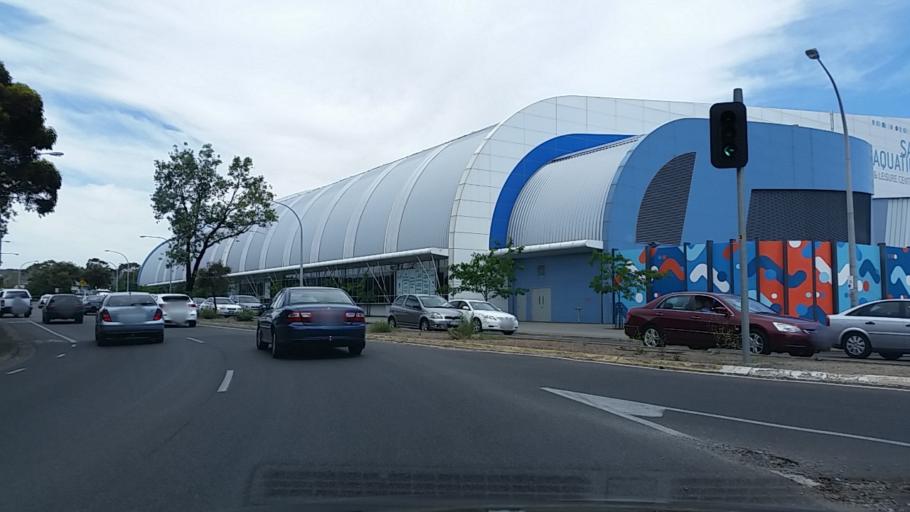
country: AU
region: South Australia
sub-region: Marion
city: Sturt
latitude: -35.0117
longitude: 138.5407
